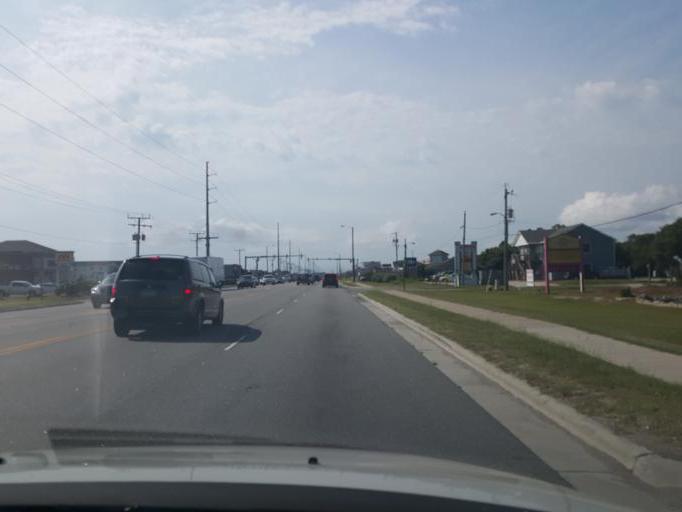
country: US
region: North Carolina
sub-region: Dare County
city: Kill Devil Hills
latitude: 36.0059
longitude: -75.6564
